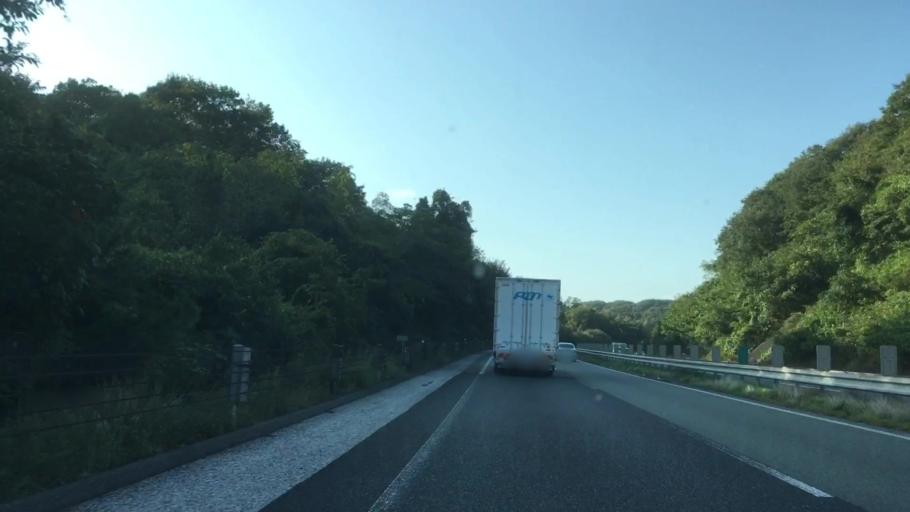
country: JP
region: Yamaguchi
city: Ogori-shimogo
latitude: 34.1613
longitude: 131.3289
